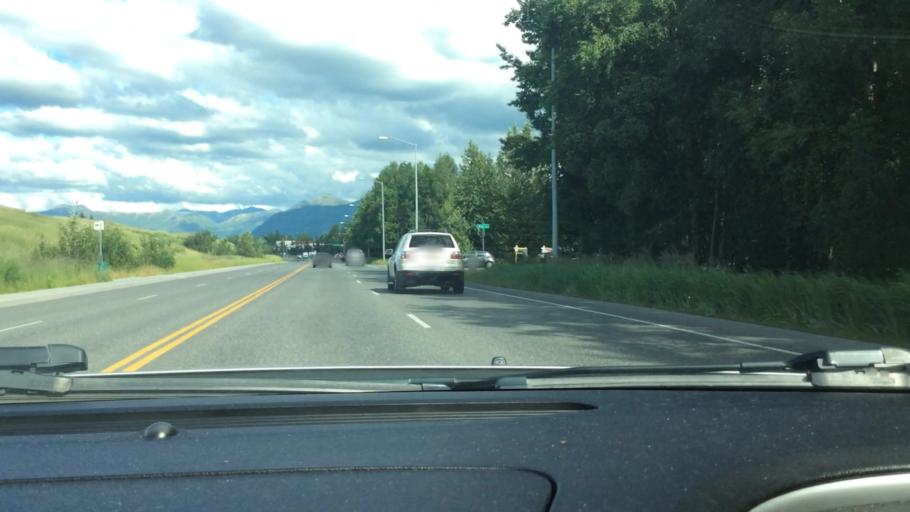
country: US
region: Alaska
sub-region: Anchorage Municipality
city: Anchorage
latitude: 61.2077
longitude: -149.8470
